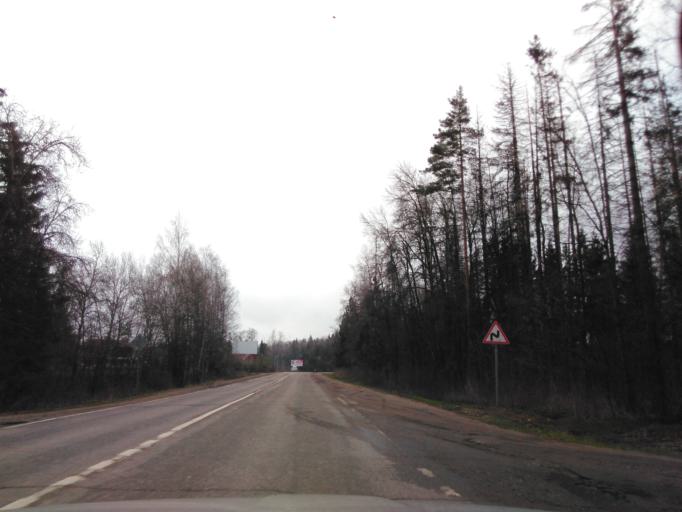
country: RU
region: Moskovskaya
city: Rozhdestveno
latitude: 55.8354
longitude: 37.0167
